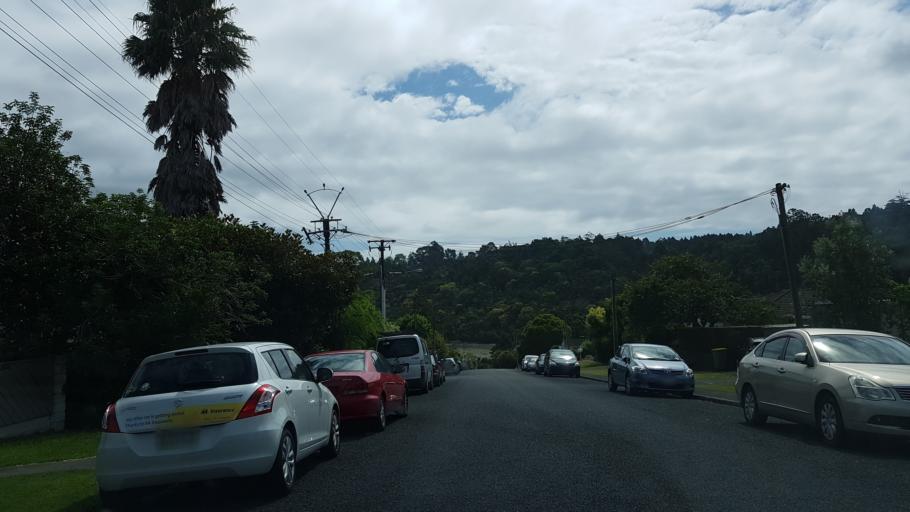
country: NZ
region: Auckland
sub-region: Auckland
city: North Shore
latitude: -36.7792
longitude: 174.7004
